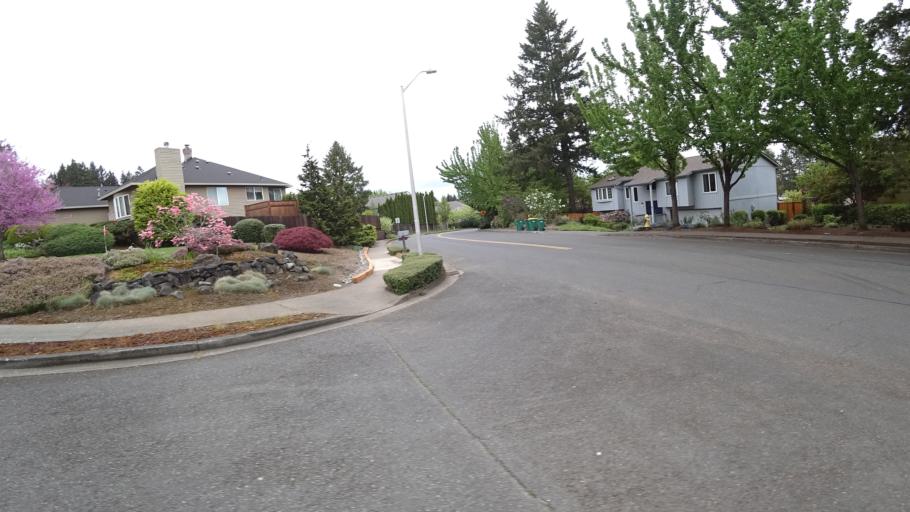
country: US
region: Oregon
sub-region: Washington County
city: Beaverton
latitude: 45.4582
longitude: -122.8190
